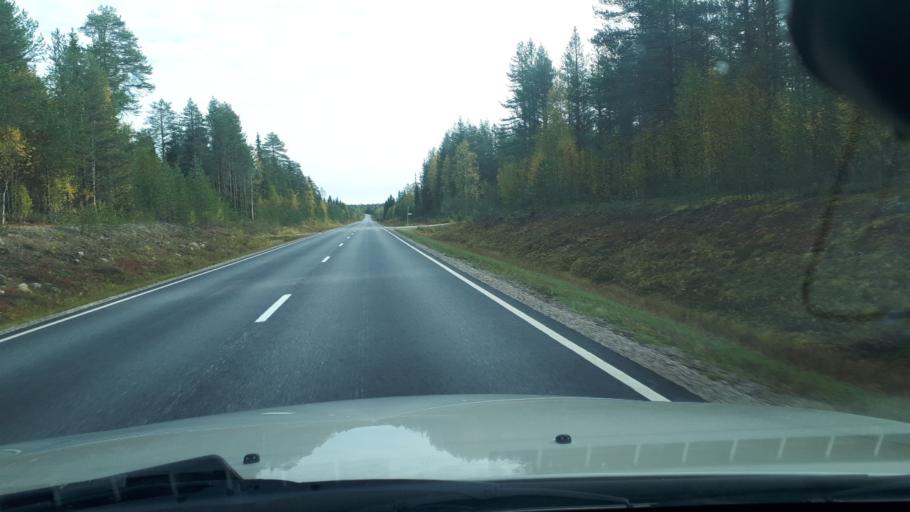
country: FI
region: Northern Ostrobothnia
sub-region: Oulu
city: Yli-Ii
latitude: 65.9253
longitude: 25.8225
